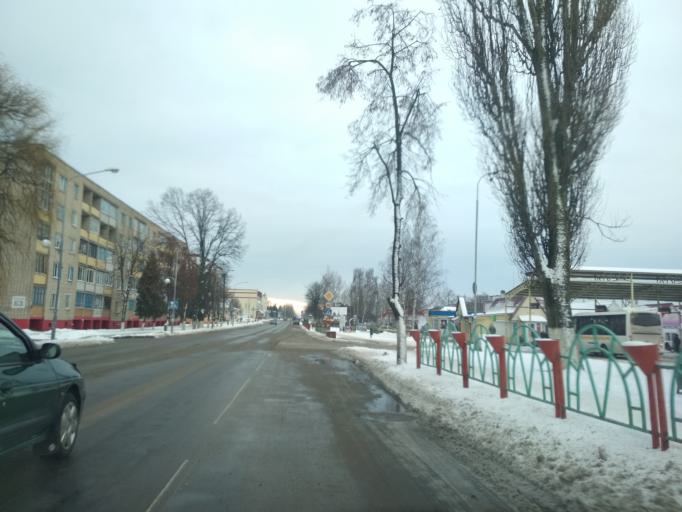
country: BY
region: Minsk
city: Mar''ina Horka
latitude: 53.5131
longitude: 28.1425
